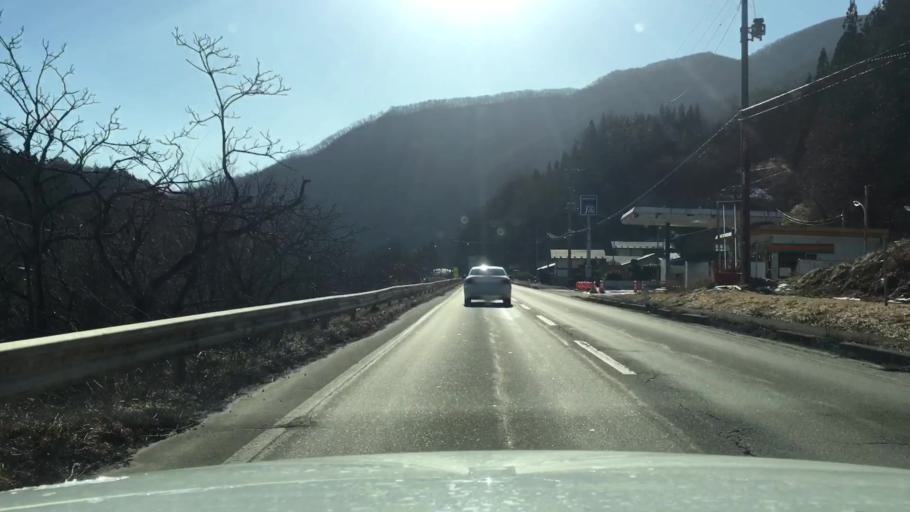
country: JP
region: Iwate
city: Tono
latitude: 39.6177
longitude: 141.6238
